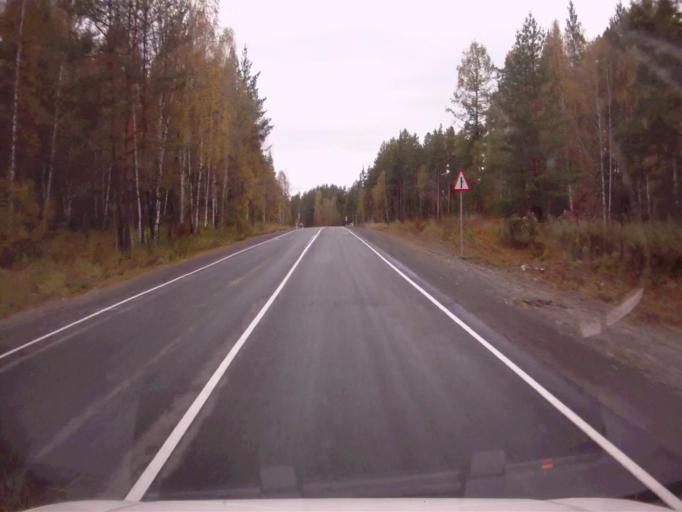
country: RU
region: Chelyabinsk
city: Nyazepetrovsk
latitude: 56.0598
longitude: 59.7313
